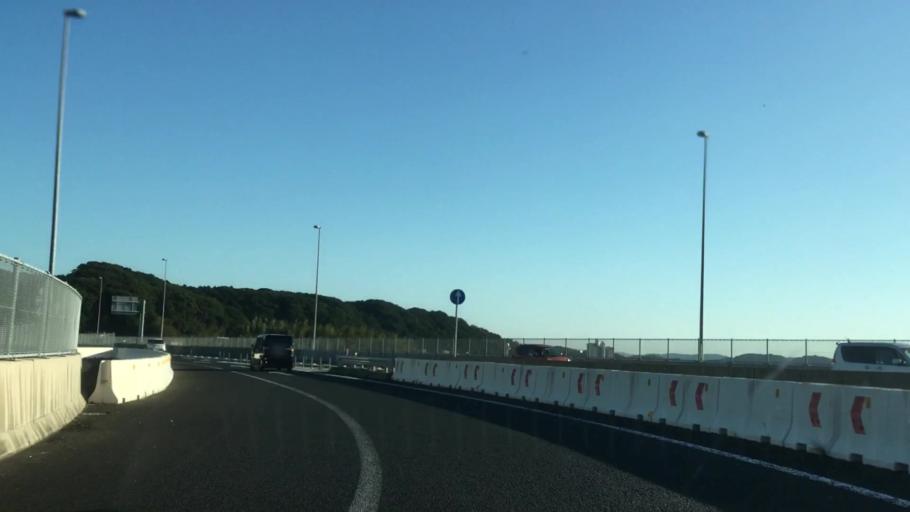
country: JP
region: Nagasaki
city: Sasebo
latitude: 33.2018
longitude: 129.6734
